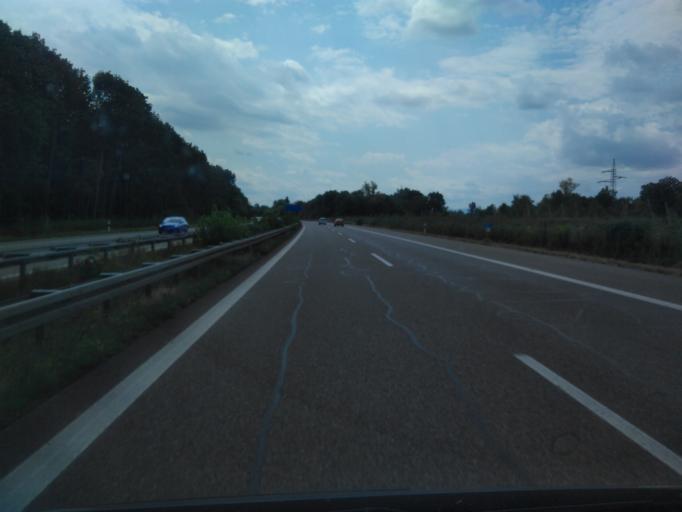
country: FR
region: Alsace
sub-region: Departement du Haut-Rhin
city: Kembs
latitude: 47.6702
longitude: 7.5238
